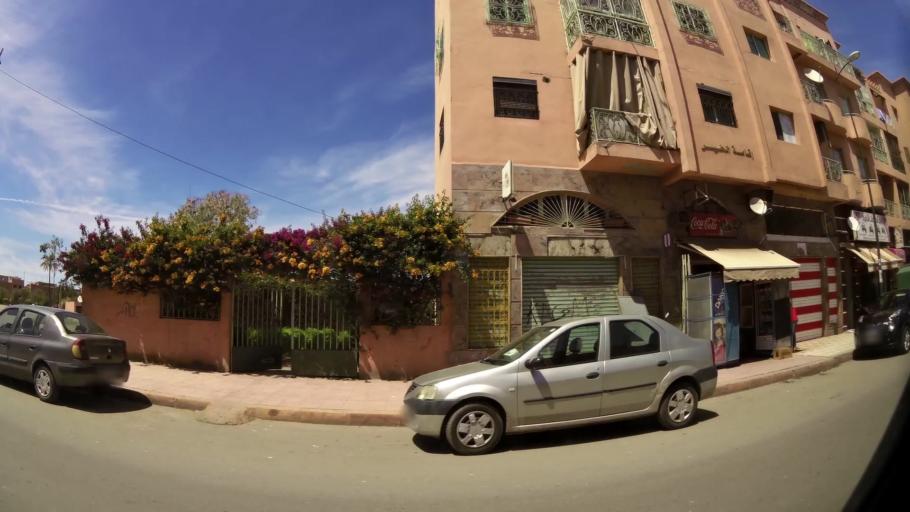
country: MA
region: Marrakech-Tensift-Al Haouz
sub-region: Marrakech
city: Marrakesh
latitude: 31.6596
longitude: -7.9994
